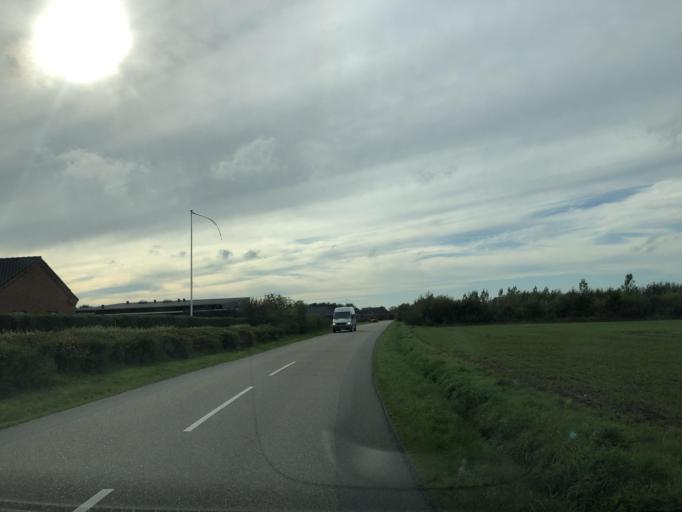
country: DK
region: Central Jutland
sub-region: Ringkobing-Skjern Kommune
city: Ringkobing
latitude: 56.0959
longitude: 8.2751
